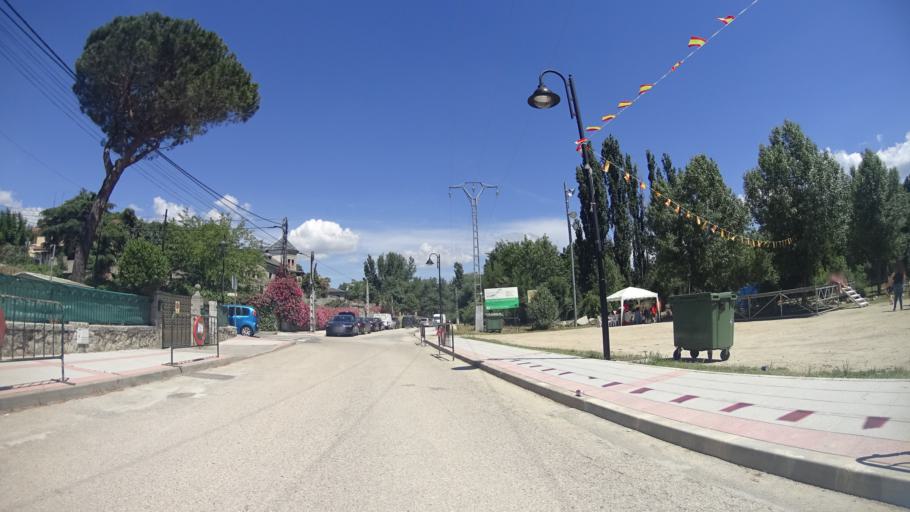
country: ES
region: Madrid
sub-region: Provincia de Madrid
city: Galapagar
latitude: 40.5990
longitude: -3.9845
